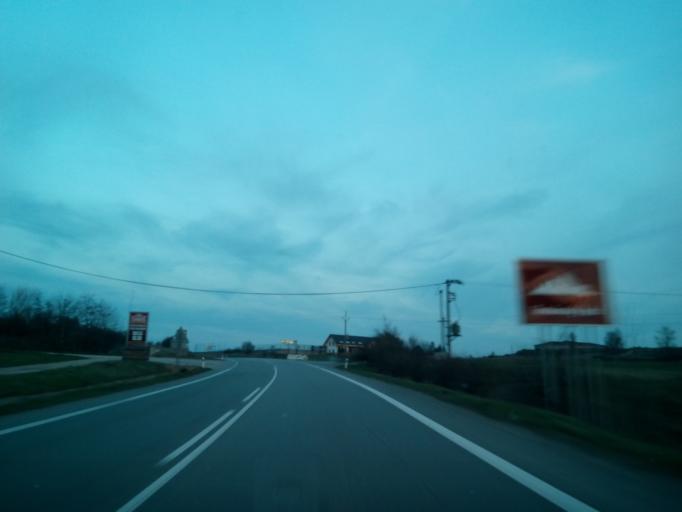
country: SK
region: Kosicky
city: Medzev
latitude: 48.6062
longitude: 20.8708
